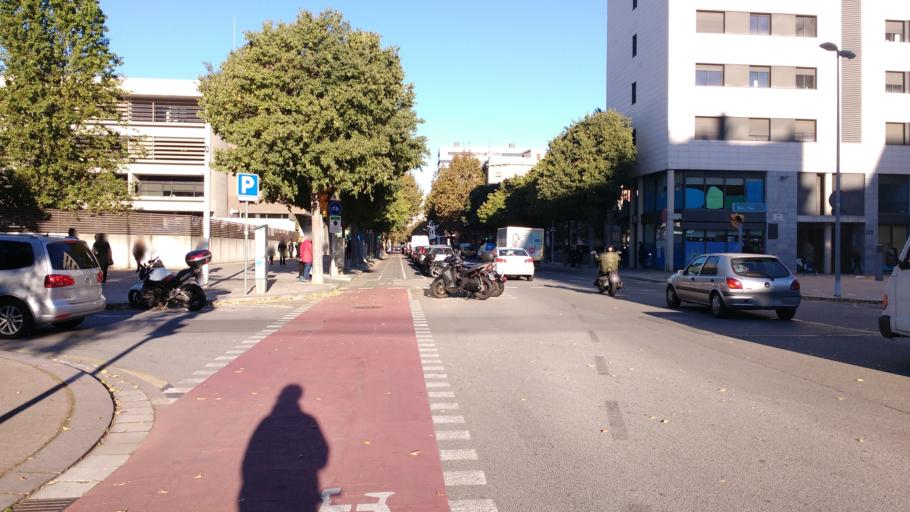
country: ES
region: Catalonia
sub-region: Provincia de Barcelona
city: Sant Marti
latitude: 41.4026
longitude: 2.2104
